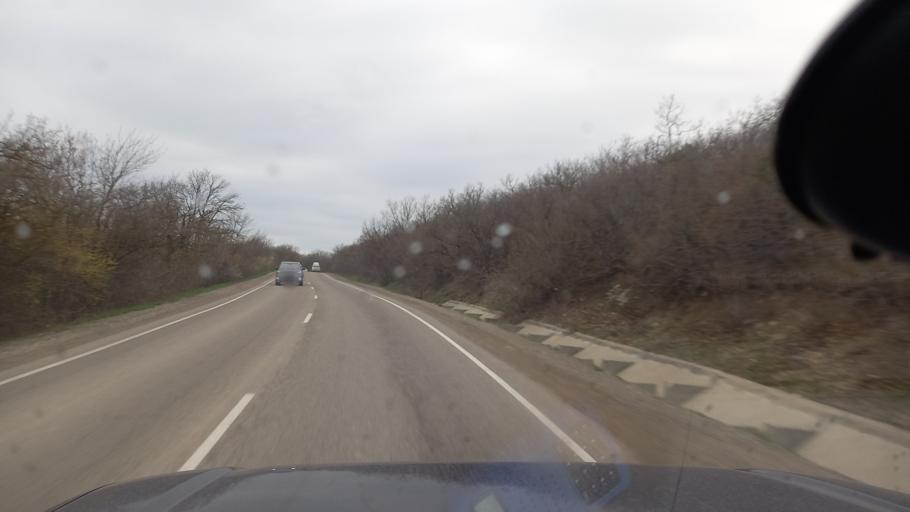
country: RU
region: Krasnodarskiy
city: Sukko
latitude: 44.8410
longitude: 37.4142
